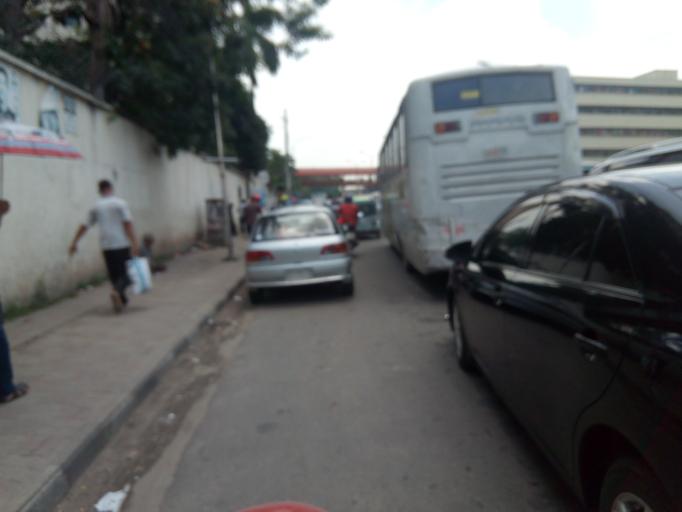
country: BD
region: Dhaka
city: Azimpur
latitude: 23.7402
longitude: 90.3962
